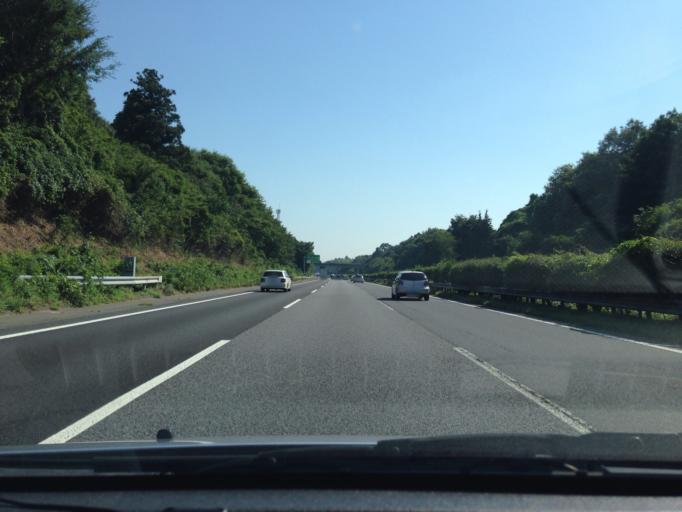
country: JP
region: Ibaraki
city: Ishioka
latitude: 36.1660
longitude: 140.2365
